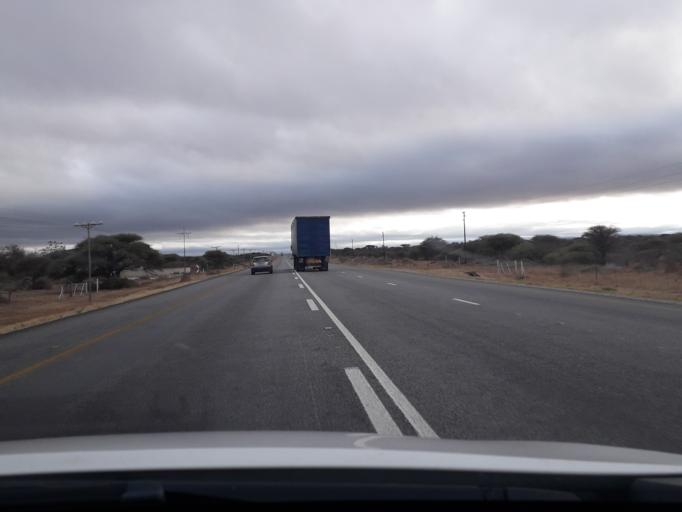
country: ZA
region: Limpopo
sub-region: Capricorn District Municipality
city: Polokwane
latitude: -23.7392
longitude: 29.5748
